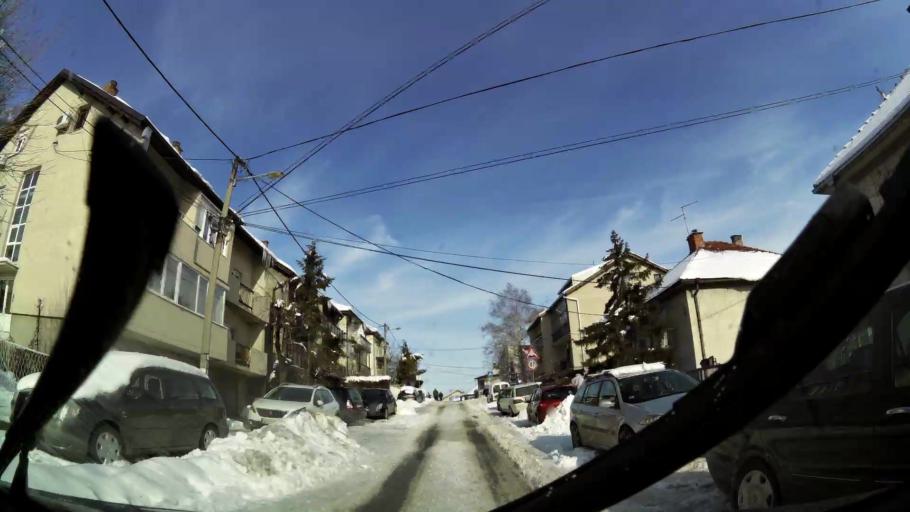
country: RS
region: Central Serbia
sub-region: Belgrade
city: Palilula
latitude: 44.7957
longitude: 20.5241
